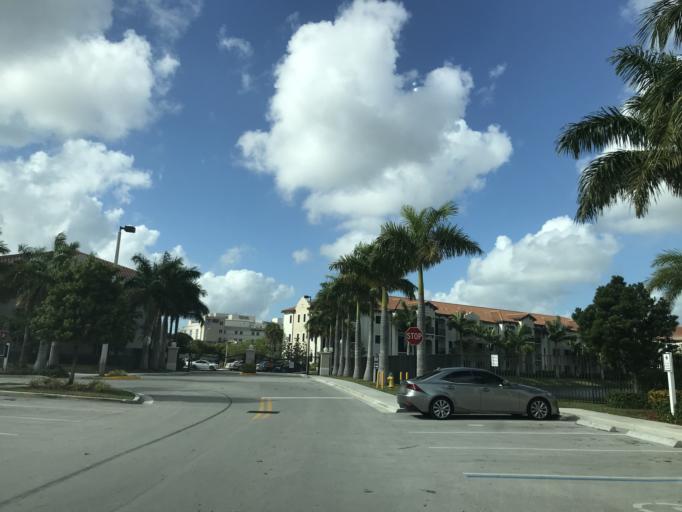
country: US
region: Florida
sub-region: Broward County
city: Margate
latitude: 26.2619
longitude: -80.1994
